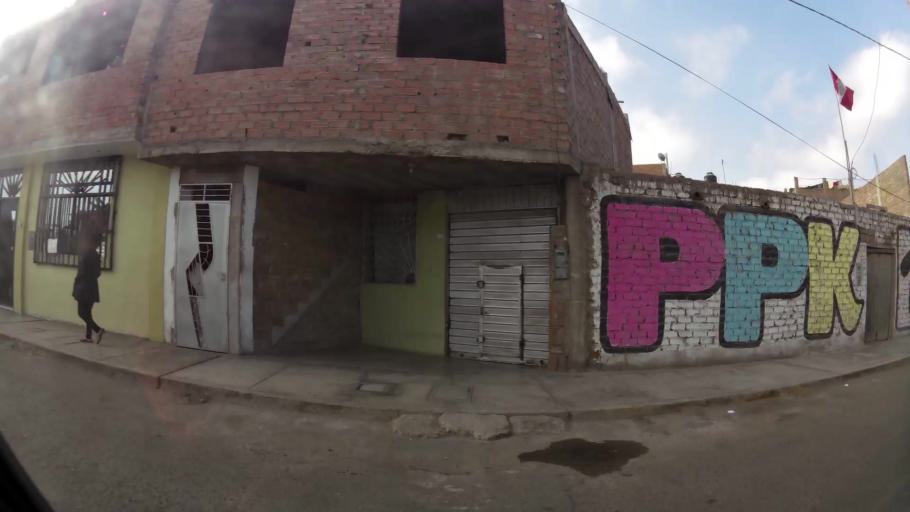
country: PE
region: La Libertad
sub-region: Provincia de Trujillo
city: El Porvenir
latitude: -8.0925
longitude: -79.0228
